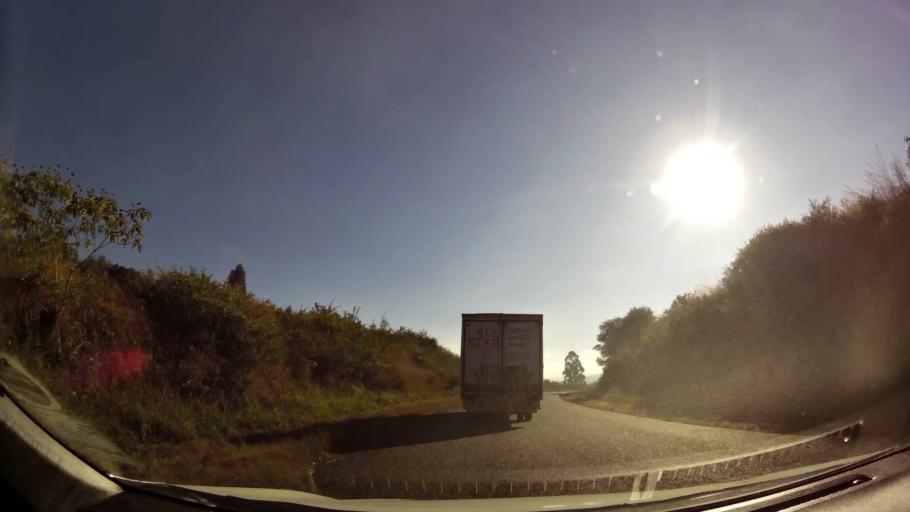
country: ZA
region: Limpopo
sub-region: Mopani District Municipality
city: Tzaneen
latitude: -23.8948
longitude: 30.0753
